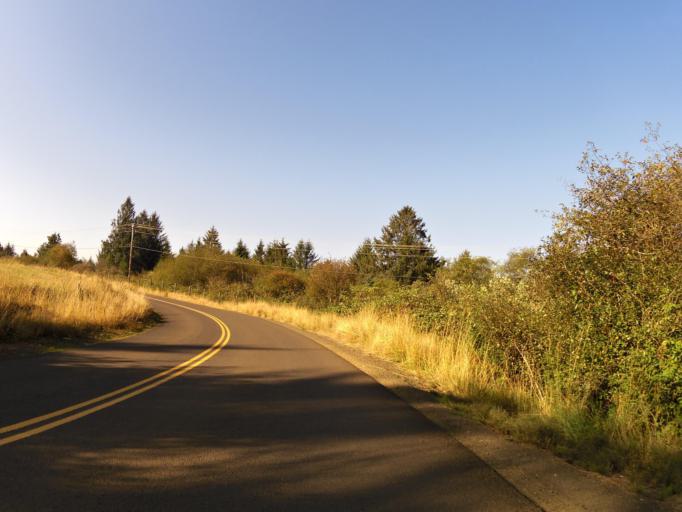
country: US
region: Oregon
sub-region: Tillamook County
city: Tillamook
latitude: 45.4053
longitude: -123.7931
